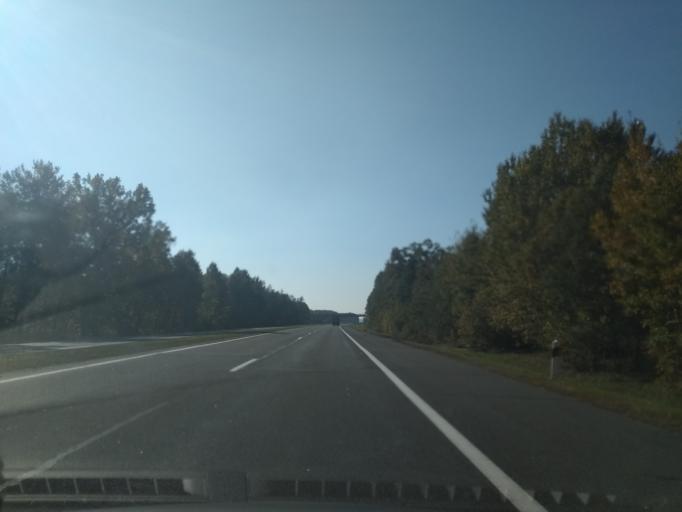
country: BY
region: Brest
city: Ivatsevichy
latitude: 52.6800
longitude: 25.3271
